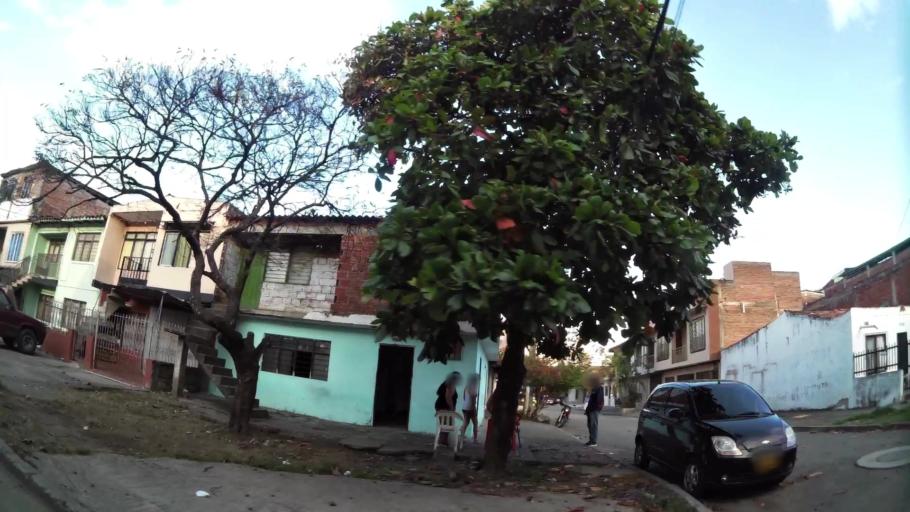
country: CO
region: Valle del Cauca
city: Cali
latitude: 3.4263
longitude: -76.5103
